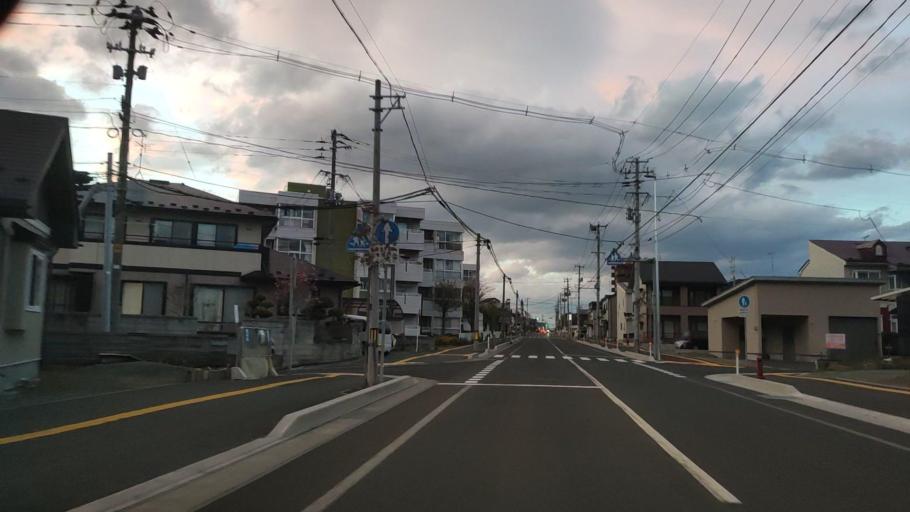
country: JP
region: Iwate
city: Morioka-shi
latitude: 39.7197
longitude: 141.1086
